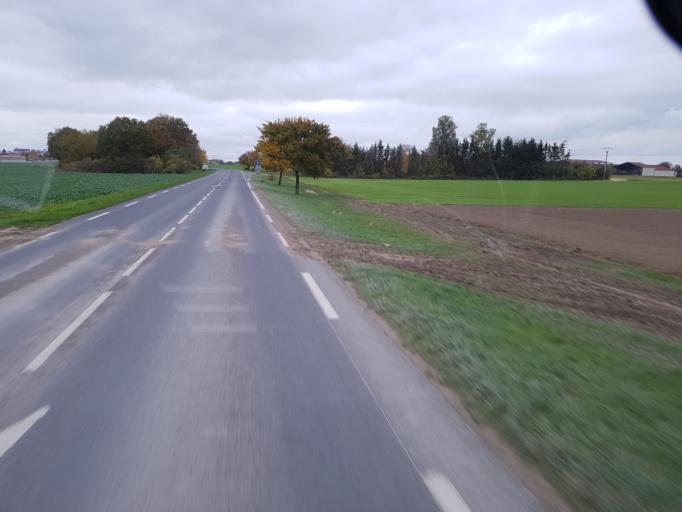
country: FR
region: Champagne-Ardenne
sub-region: Departement de la Marne
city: Saint-Just-Sauvage
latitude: 48.5871
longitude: 3.8304
